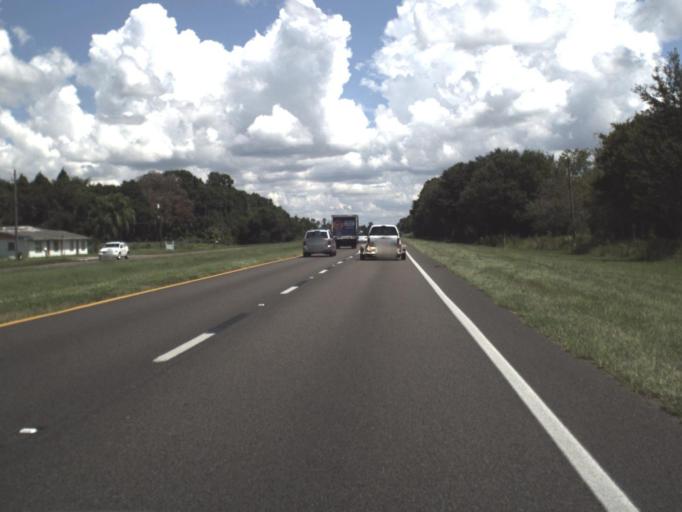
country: US
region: Florida
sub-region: Polk County
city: Fussels Corner
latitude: 28.0483
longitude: -81.8544
